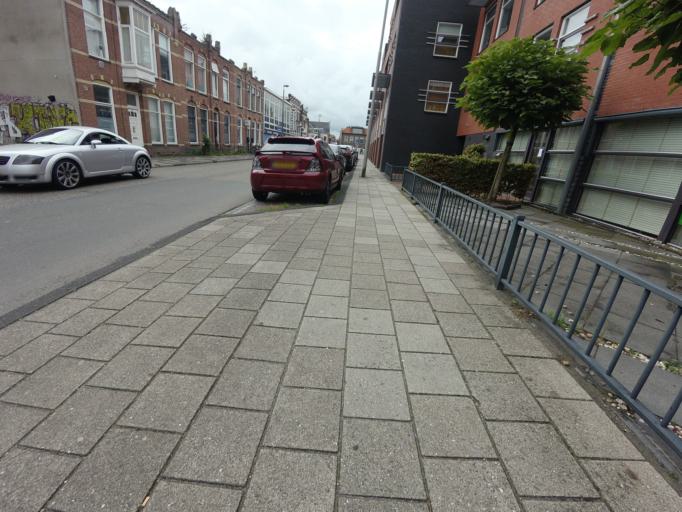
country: NL
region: Friesland
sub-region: Gemeente Leeuwarden
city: Leeuwarden
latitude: 53.2006
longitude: 5.8042
